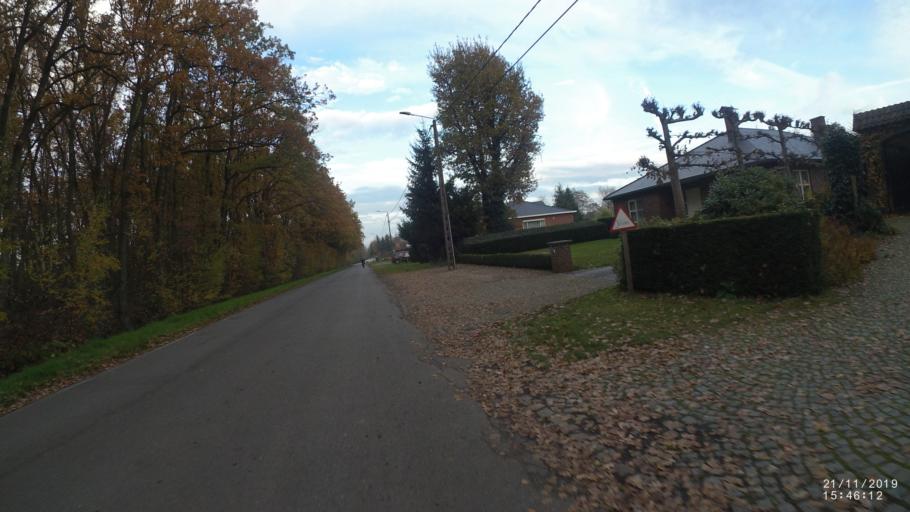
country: BE
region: Flanders
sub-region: Provincie Limburg
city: Zonhoven
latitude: 50.9750
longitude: 5.3453
